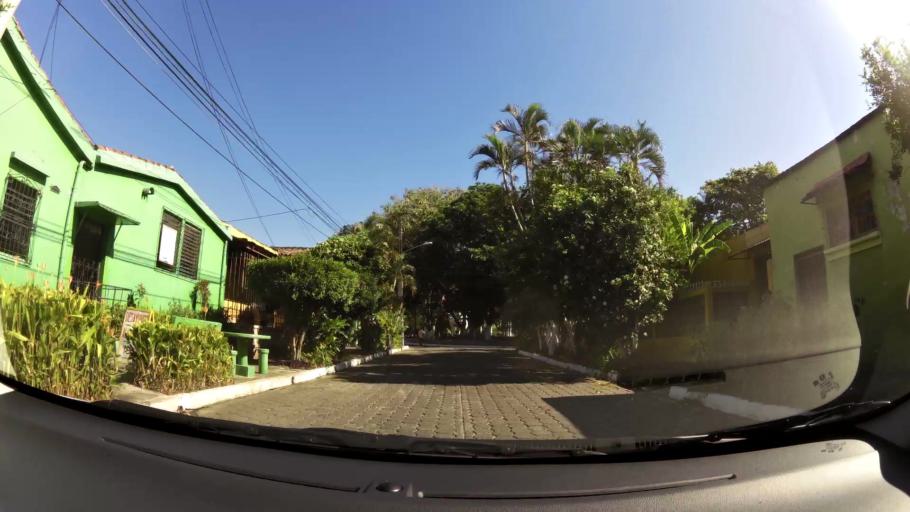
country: SV
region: Sonsonate
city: Sonzacate
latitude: 13.7284
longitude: -89.7211
